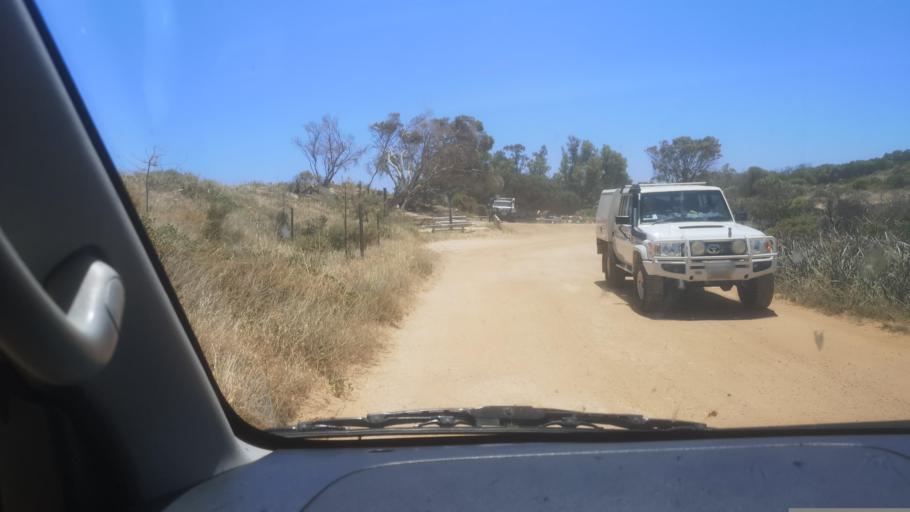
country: AU
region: Western Australia
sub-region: Dandaragan
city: Jurien Bay
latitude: -30.1823
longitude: 114.9997
